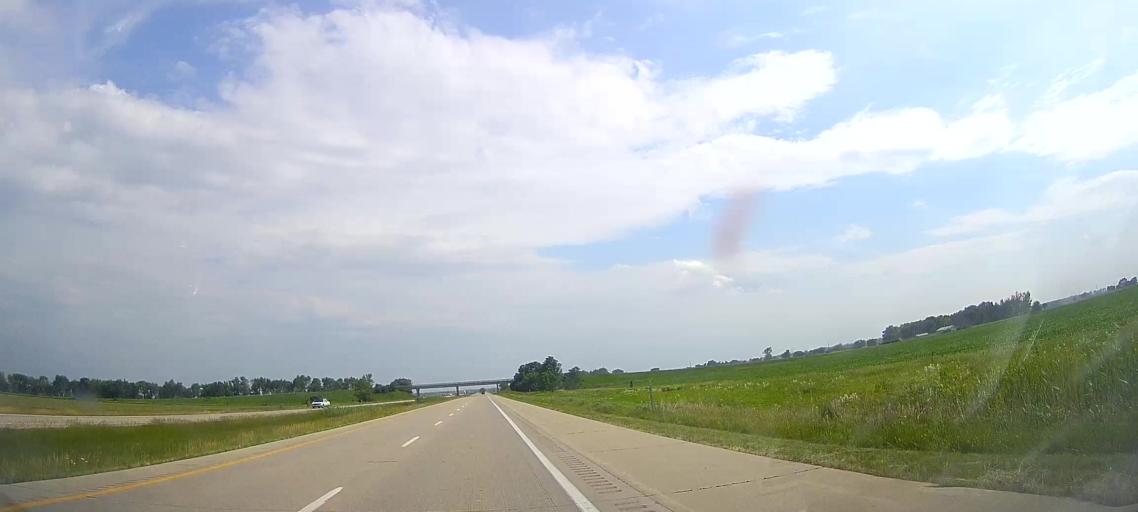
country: US
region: Iowa
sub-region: Monona County
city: Onawa
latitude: 41.8901
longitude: -96.1046
